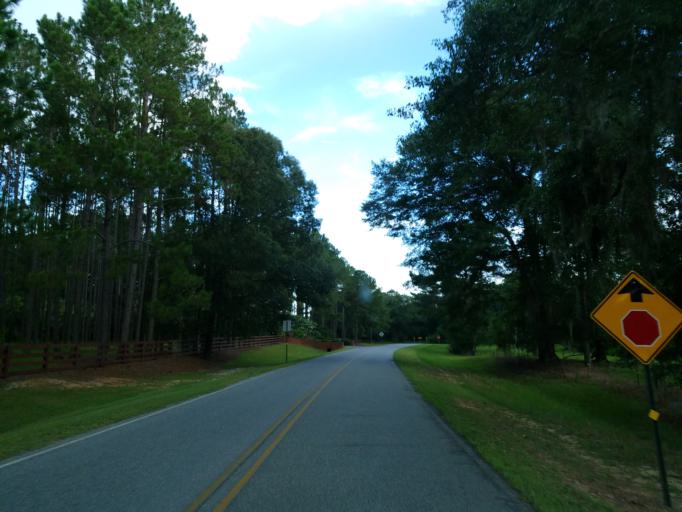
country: US
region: Georgia
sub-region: Tift County
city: Omega
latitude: 31.2569
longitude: -83.5134
